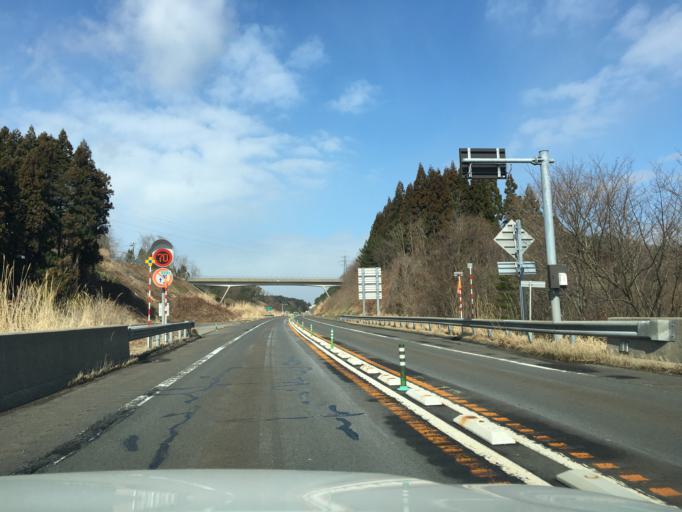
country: JP
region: Akita
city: Akita
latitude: 39.7569
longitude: 140.1358
